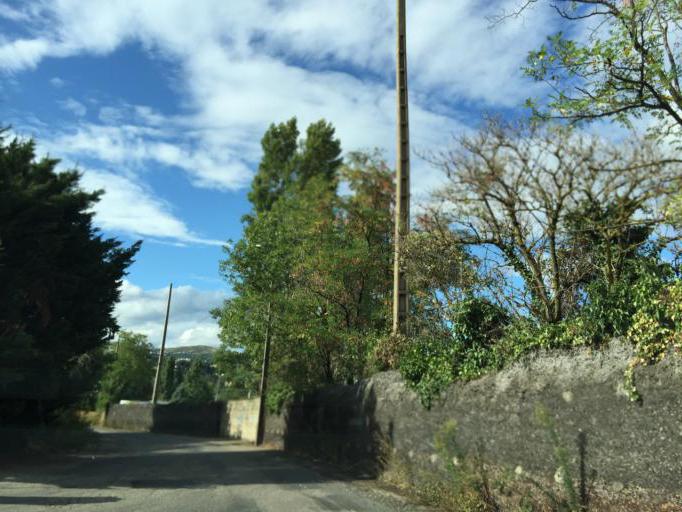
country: FR
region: Rhone-Alpes
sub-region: Departement de la Loire
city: La Grand-Croix
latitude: 45.4867
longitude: 4.5531
